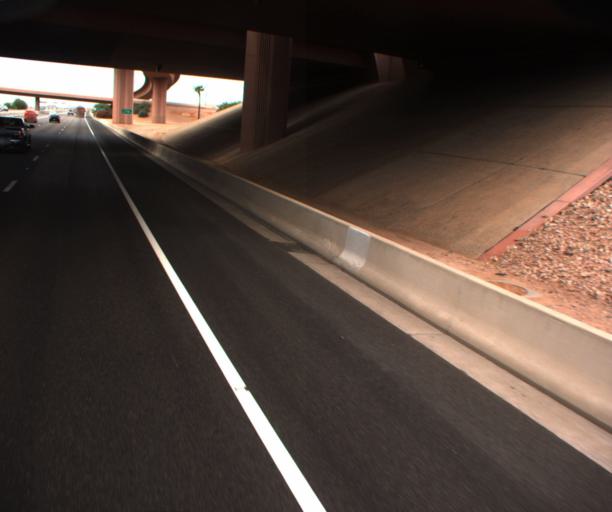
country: US
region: Arizona
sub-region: Maricopa County
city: Tempe
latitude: 33.4341
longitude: -111.8906
